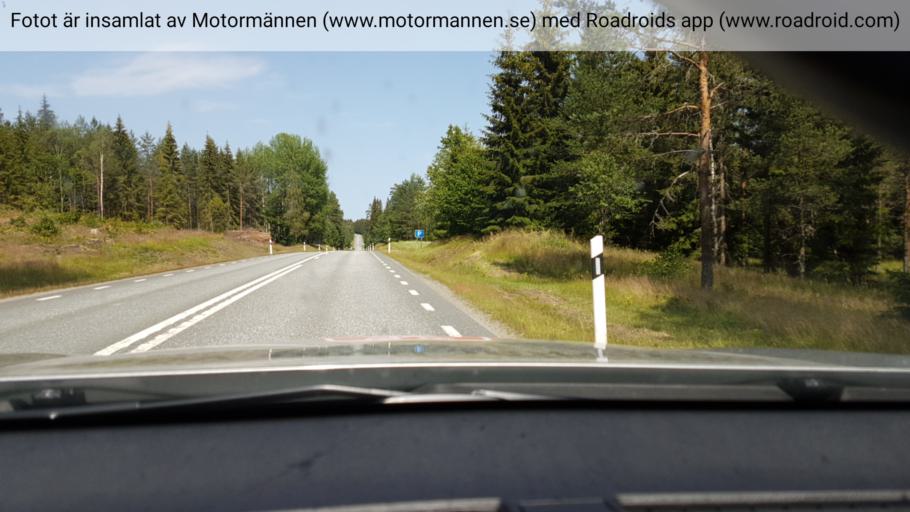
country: SE
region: Joenkoeping
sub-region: Nassjo Kommun
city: Bodafors
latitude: 57.5488
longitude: 14.7916
